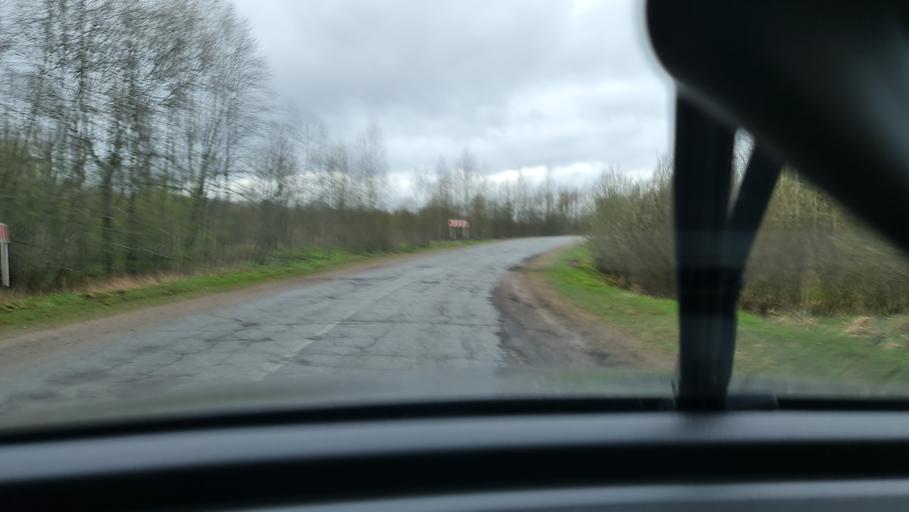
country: RU
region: Novgorod
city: Marevo
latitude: 57.2453
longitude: 32.0622
